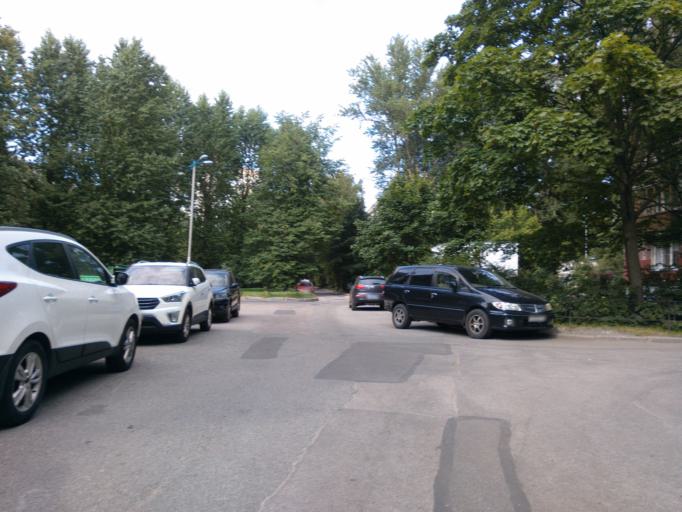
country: RU
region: Leningrad
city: Akademicheskoe
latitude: 60.0222
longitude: 30.3941
